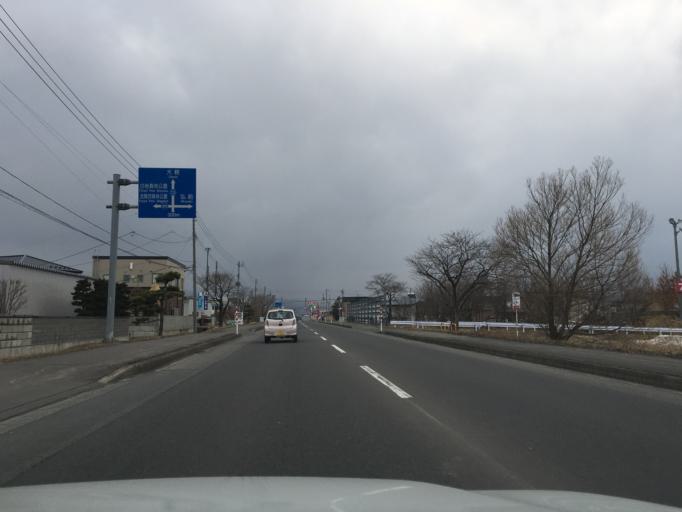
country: JP
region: Aomori
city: Kuroishi
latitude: 40.5892
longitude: 140.5690
